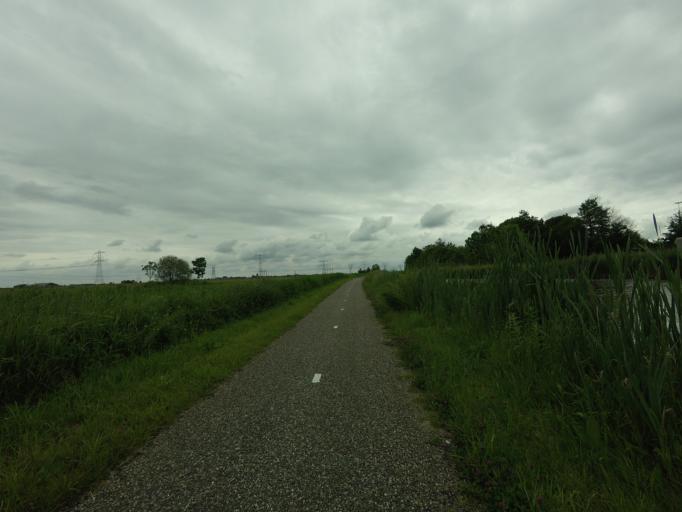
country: NL
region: North Holland
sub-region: Gemeente Waterland
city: Broek in Waterland
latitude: 52.4015
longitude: 4.9611
